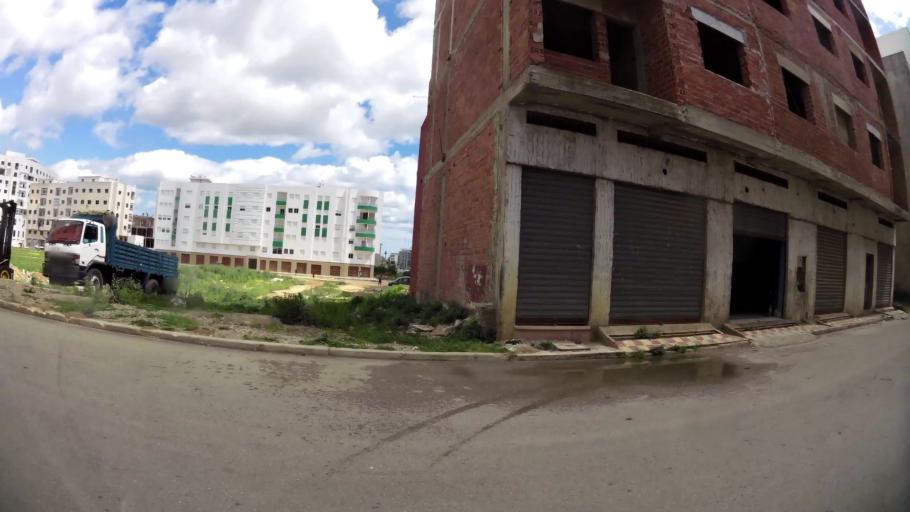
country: MA
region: Tanger-Tetouan
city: Tetouan
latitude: 35.5875
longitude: -5.3438
